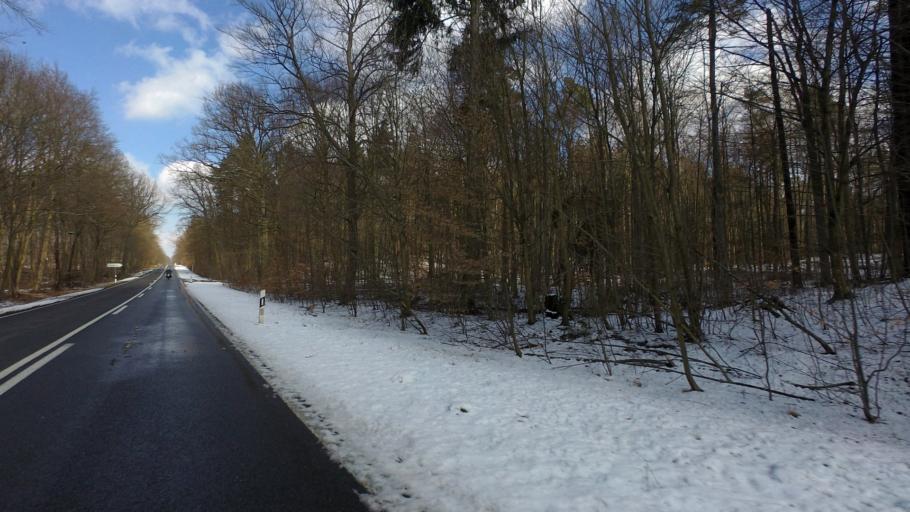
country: DE
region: Brandenburg
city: Eberswalde
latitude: 52.8100
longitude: 13.8343
